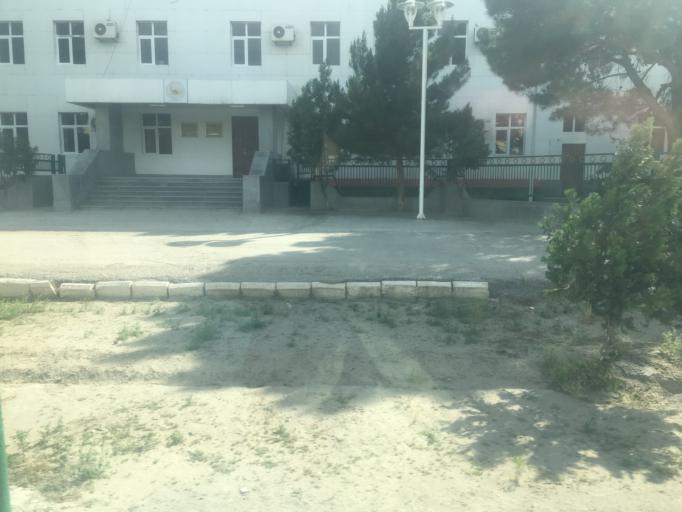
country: TM
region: Balkan
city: Balkanabat
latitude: 39.5095
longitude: 54.3580
